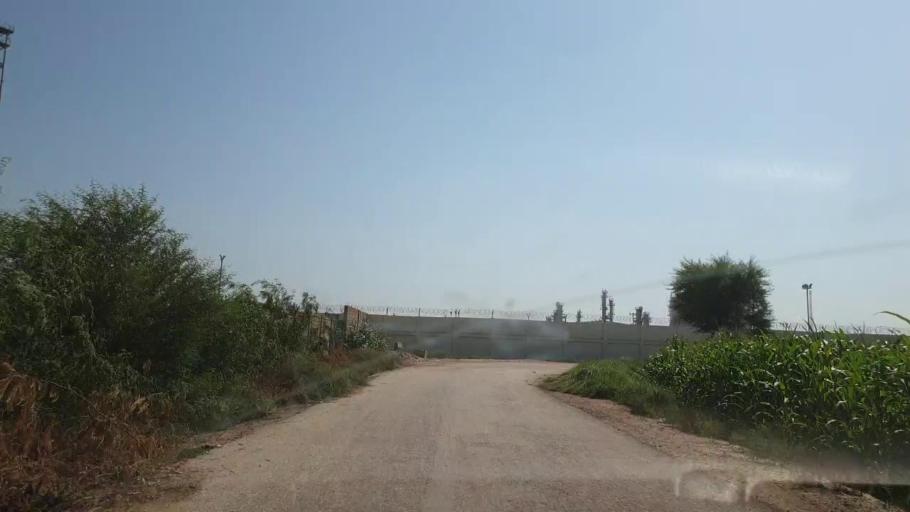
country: PK
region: Sindh
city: Tando Jam
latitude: 25.3894
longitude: 68.5820
